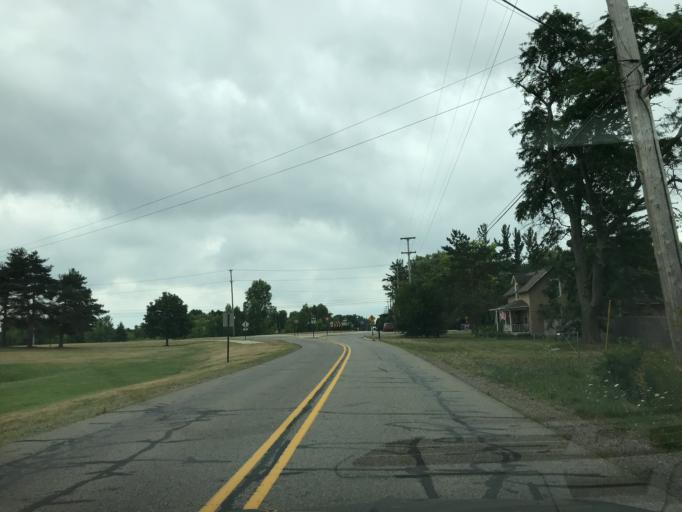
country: US
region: Michigan
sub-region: Eaton County
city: Waverly
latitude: 42.7567
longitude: -84.6618
